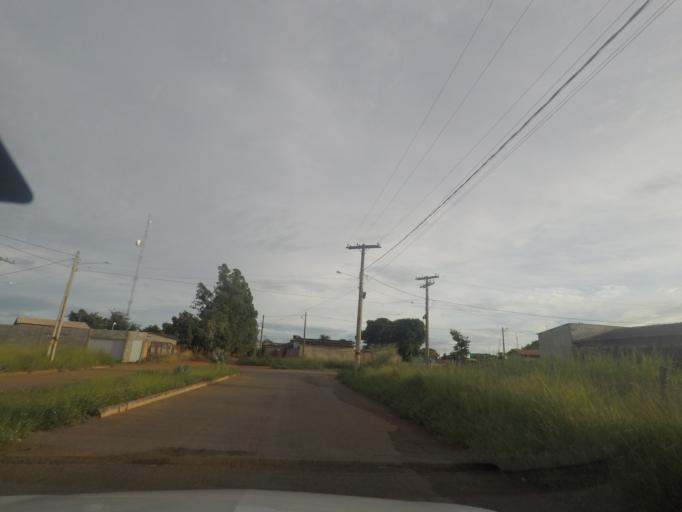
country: BR
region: Goias
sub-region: Trindade
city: Trindade
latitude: -16.7208
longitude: -49.4398
